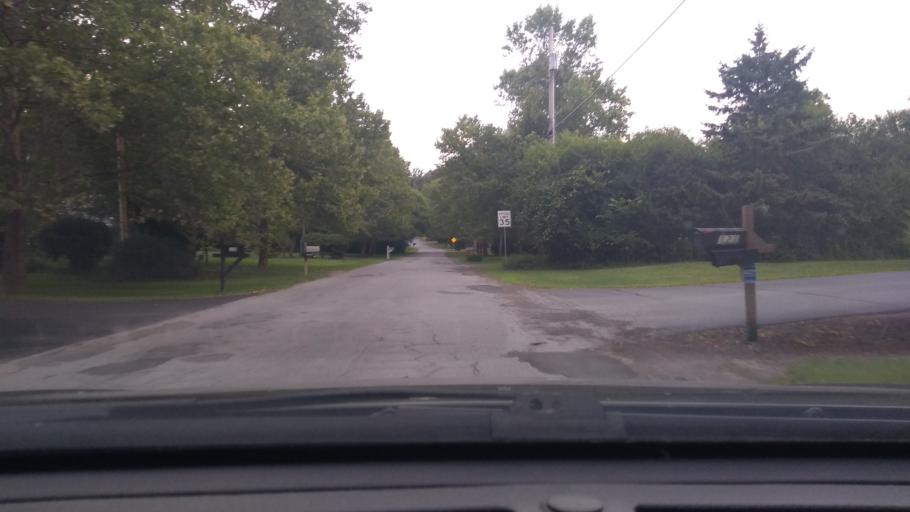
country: US
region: New York
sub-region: Erie County
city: East Aurora
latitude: 42.7739
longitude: -78.6170
